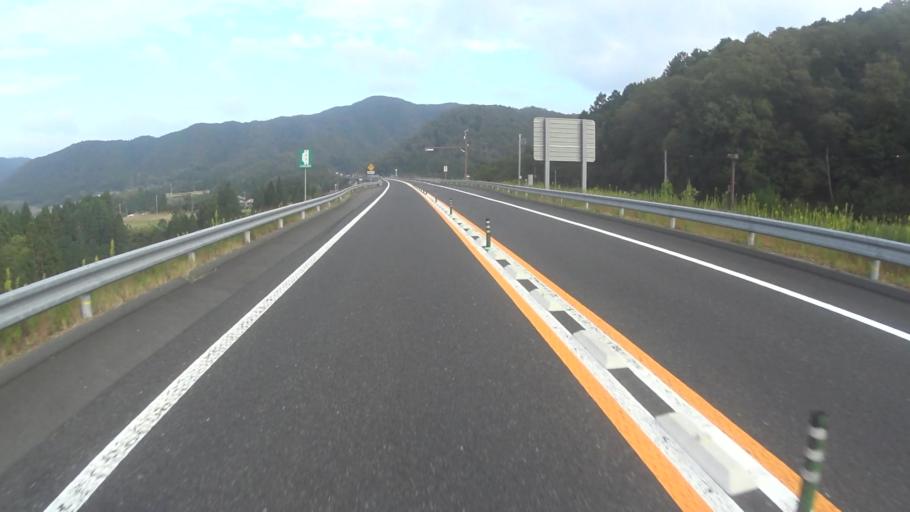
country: JP
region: Kyoto
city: Ayabe
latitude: 35.2920
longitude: 135.3355
